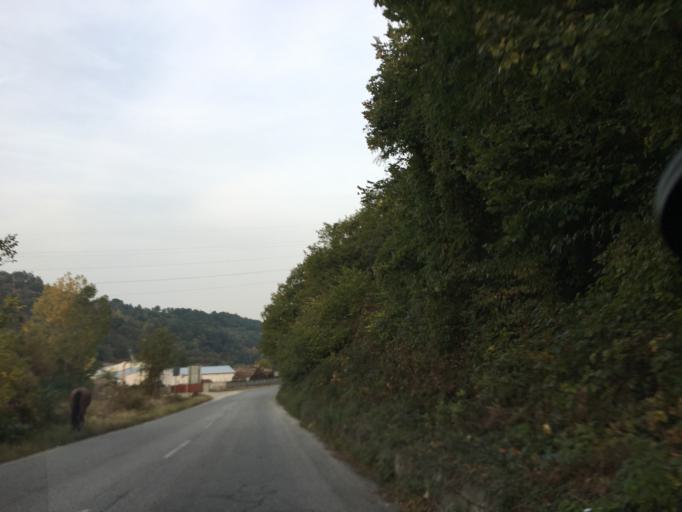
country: BG
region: Pazardzhik
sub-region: Obshtina Belovo
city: Belovo
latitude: 42.2062
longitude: 23.9997
